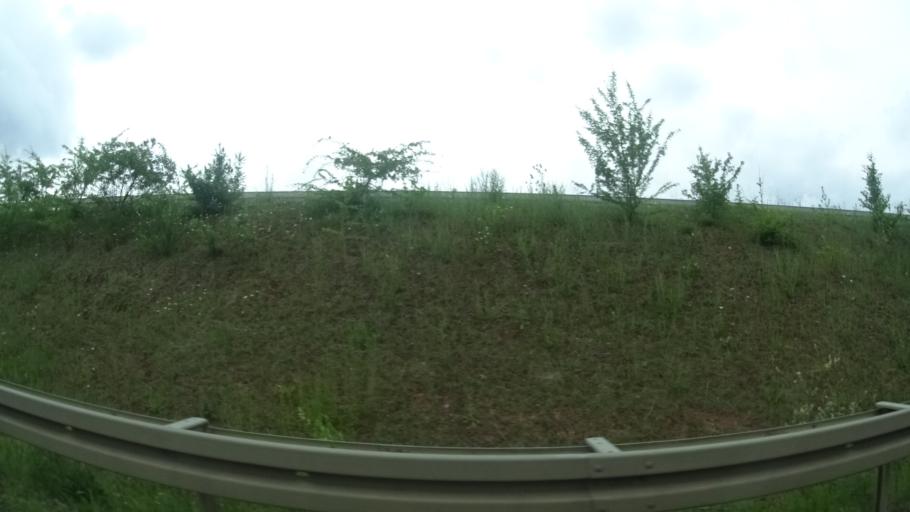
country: DE
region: Hesse
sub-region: Regierungsbezirk Kassel
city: Fulda
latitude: 50.5306
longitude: 9.6291
